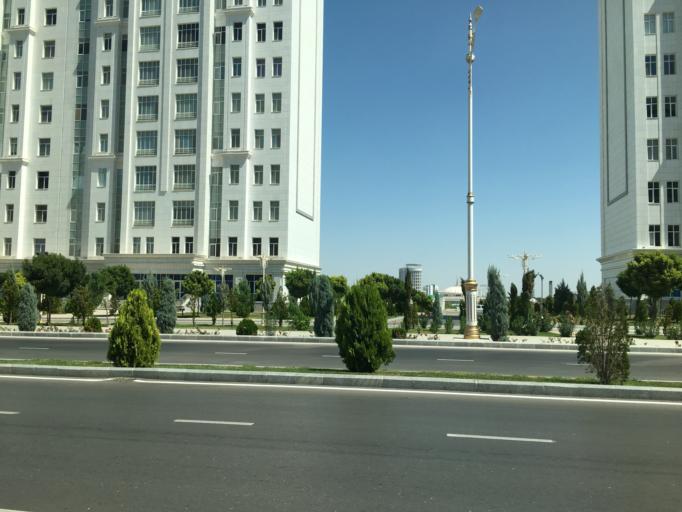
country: TM
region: Ahal
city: Ashgabat
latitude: 37.9321
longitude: 58.3680
